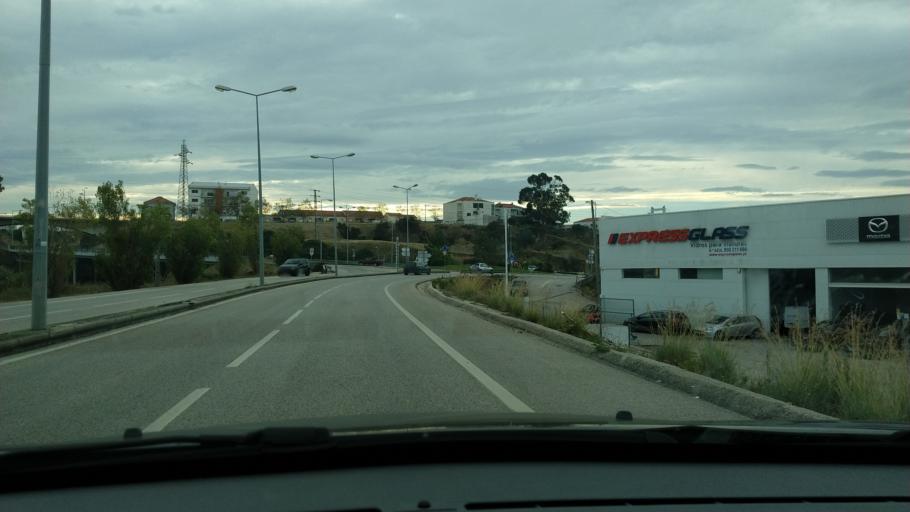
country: PT
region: Coimbra
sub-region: Figueira da Foz
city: Figueira da Foz
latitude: 40.1531
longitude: -8.8483
